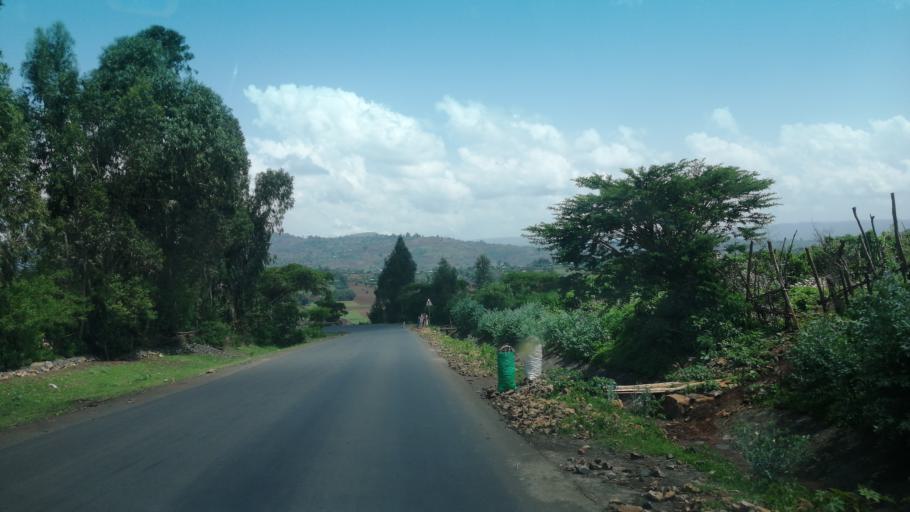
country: ET
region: Oromiya
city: Gedo
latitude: 8.9767
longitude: 37.5614
